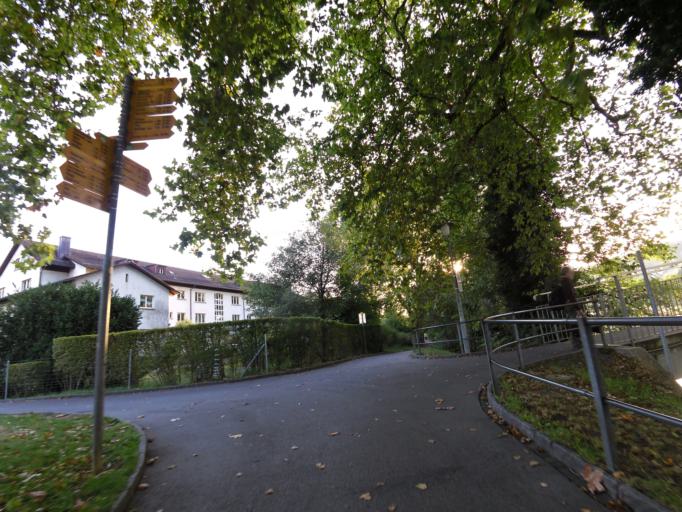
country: CH
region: Aargau
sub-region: Bezirk Aarau
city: Aarau
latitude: 47.3961
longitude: 8.0494
